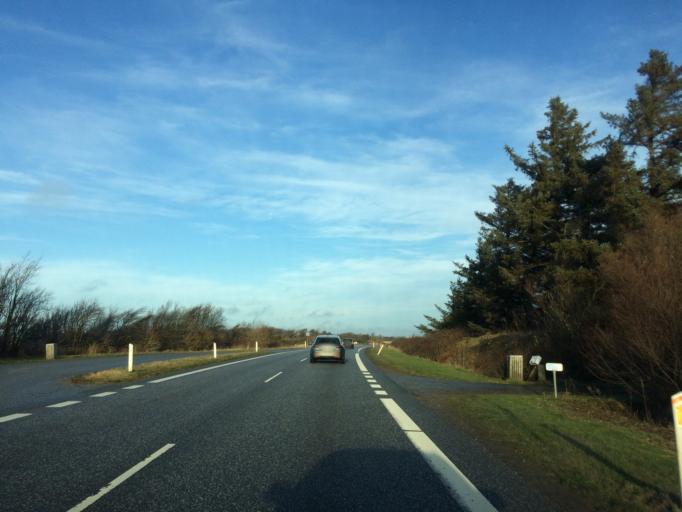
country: DK
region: North Denmark
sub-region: Thisted Kommune
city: Hurup
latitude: 56.7997
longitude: 8.4727
